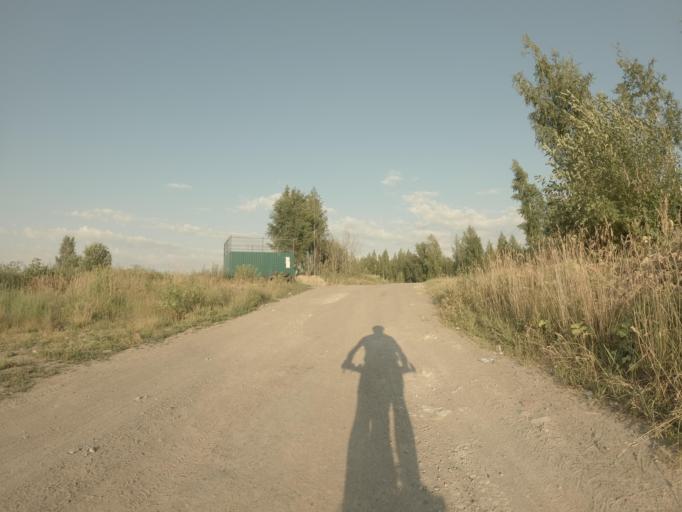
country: RU
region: Leningrad
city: Koltushi
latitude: 59.8916
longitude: 30.6939
